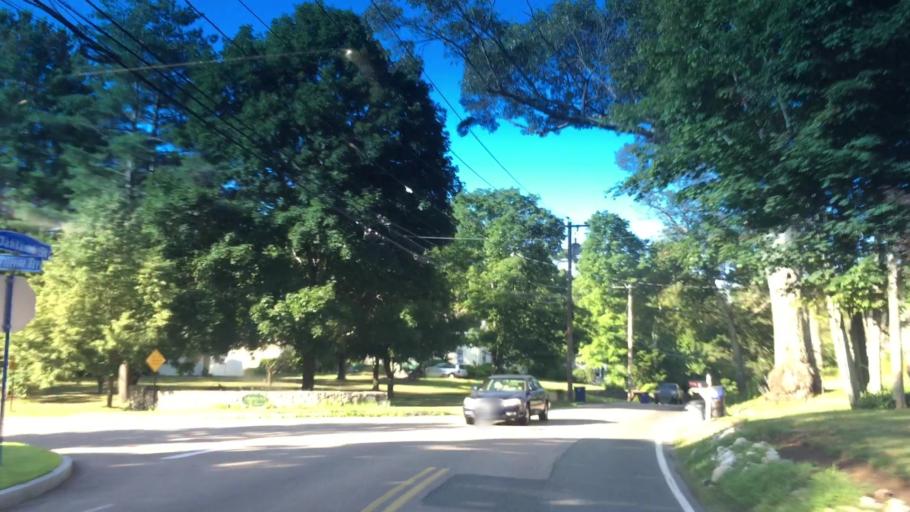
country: US
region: Massachusetts
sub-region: Norfolk County
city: Medway
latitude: 42.1436
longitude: -71.3921
